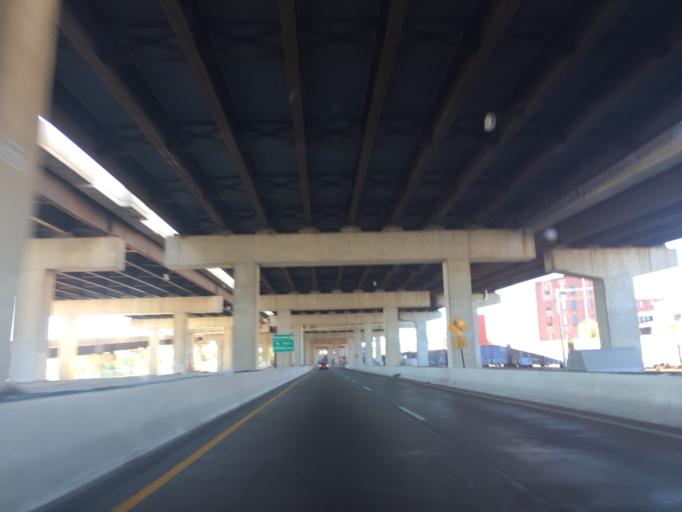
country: US
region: Maryland
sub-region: City of Baltimore
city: Baltimore
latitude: 39.2673
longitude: -76.6077
